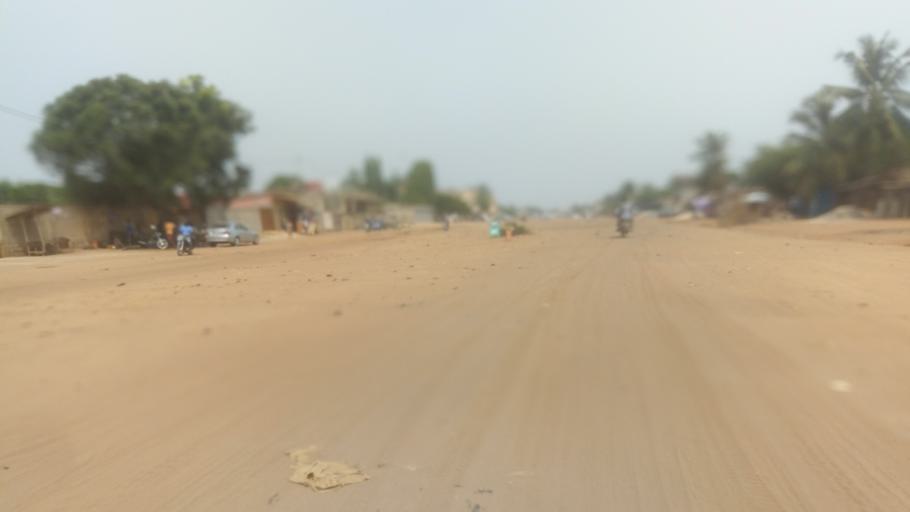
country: TG
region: Maritime
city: Lome
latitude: 6.1908
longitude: 1.1769
